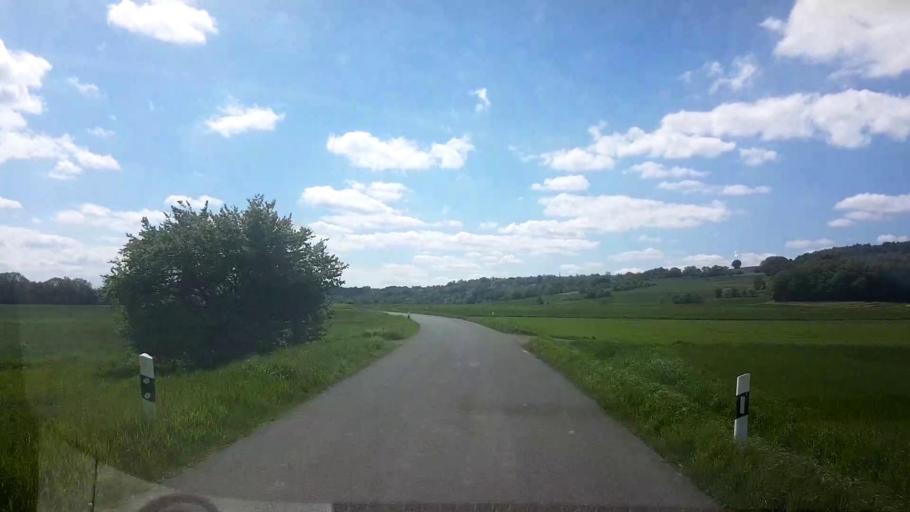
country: DE
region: Bavaria
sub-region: Upper Franconia
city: Grossheirath
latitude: 50.1553
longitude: 10.9196
